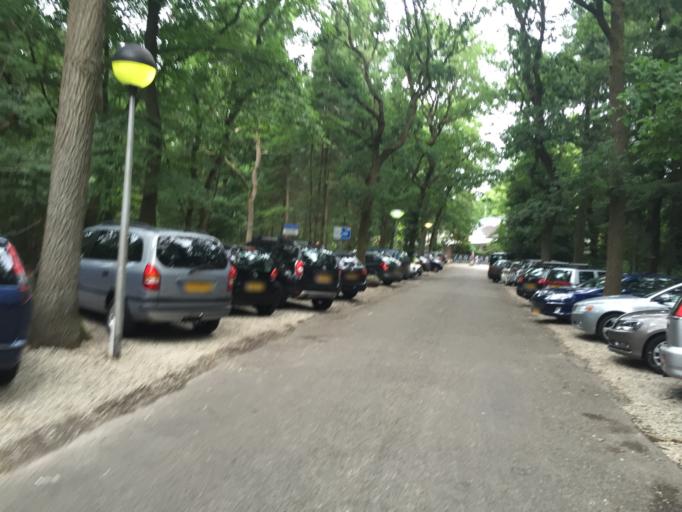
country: NL
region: Utrecht
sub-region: Gemeente Zeist
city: Zeist
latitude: 52.0874
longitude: 5.2626
